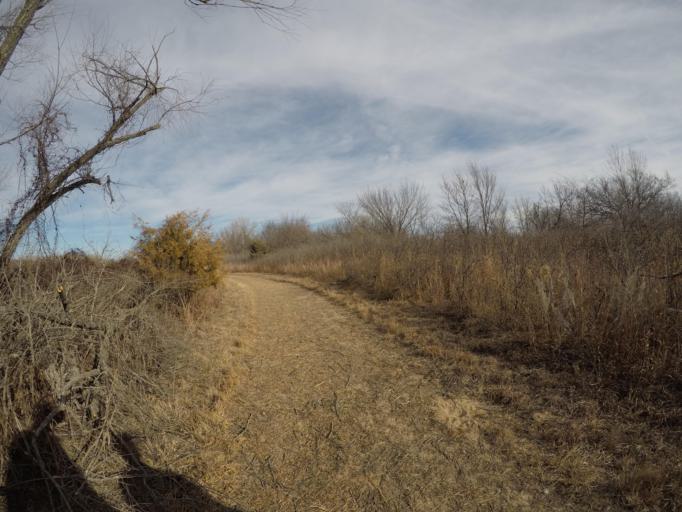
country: US
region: Kansas
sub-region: Reno County
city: Buhler
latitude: 38.1202
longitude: -97.8567
